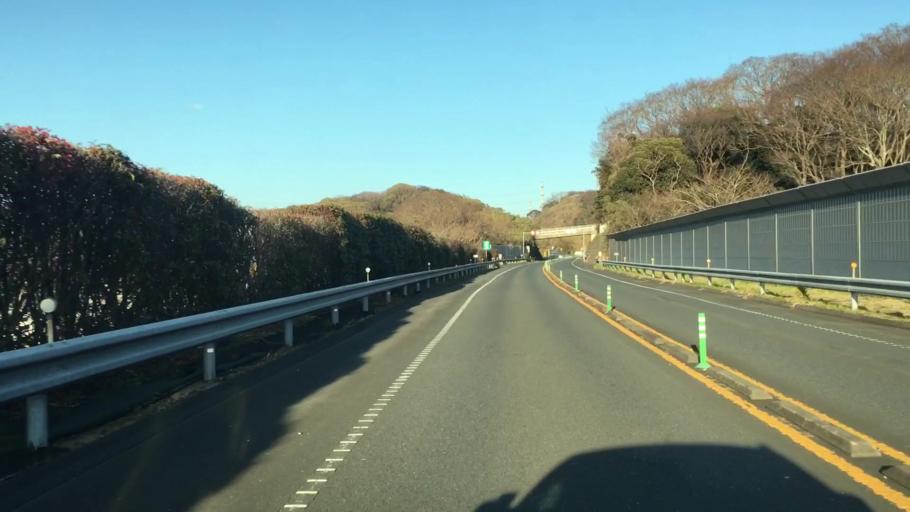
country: JP
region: Kanagawa
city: Yokosuka
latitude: 35.2295
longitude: 139.6443
